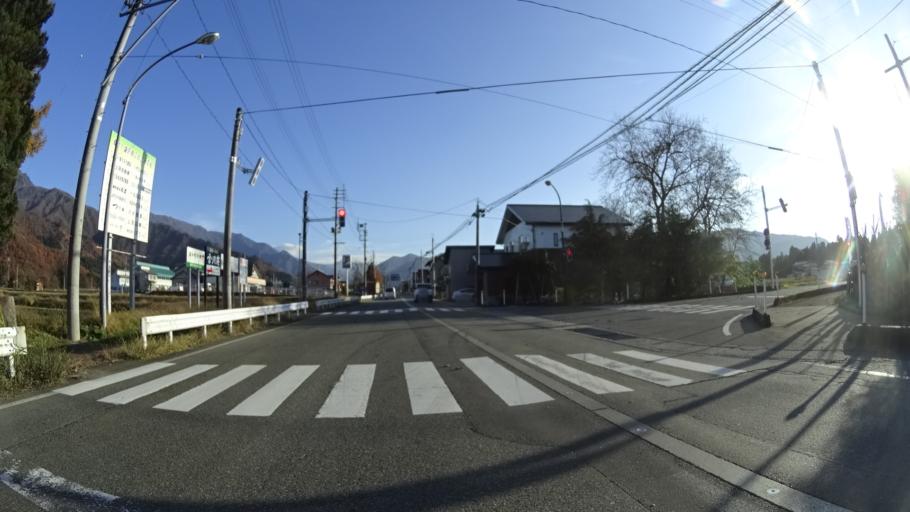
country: JP
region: Niigata
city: Shiozawa
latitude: 37.0223
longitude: 138.8650
